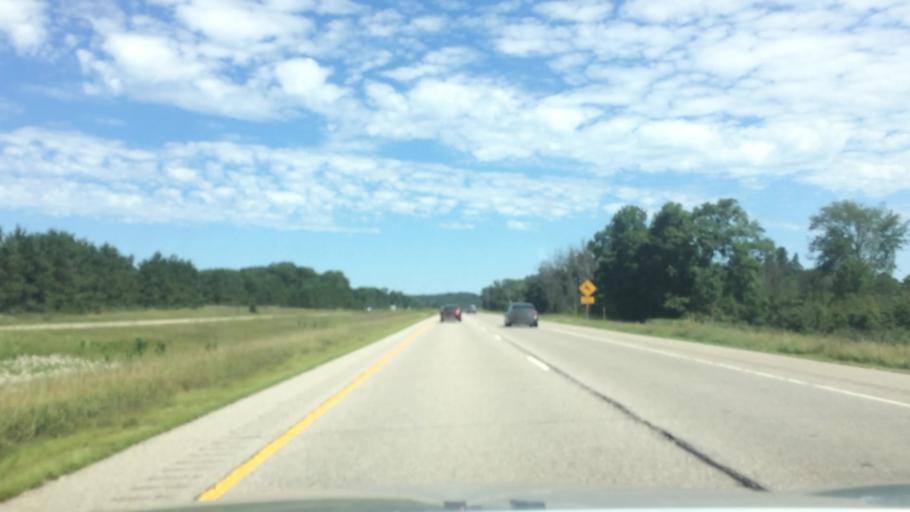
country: US
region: Wisconsin
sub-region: Marquette County
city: Westfield
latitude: 43.7602
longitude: -89.4841
